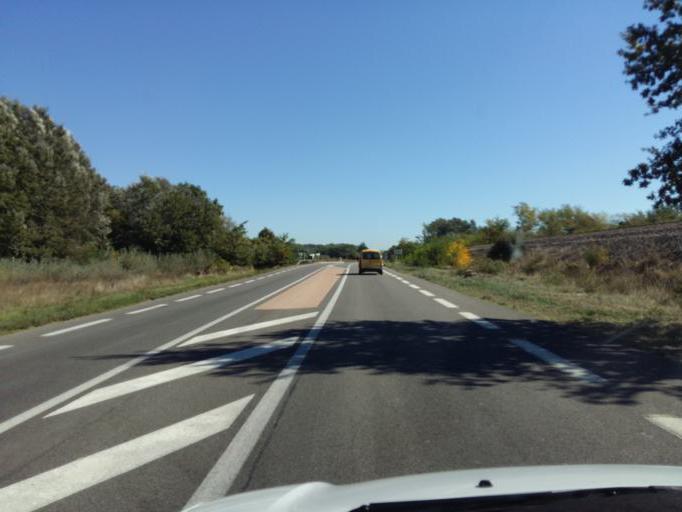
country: FR
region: Provence-Alpes-Cote d'Azur
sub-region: Departement des Bouches-du-Rhone
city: Charleval
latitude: 43.7522
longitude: 5.2575
